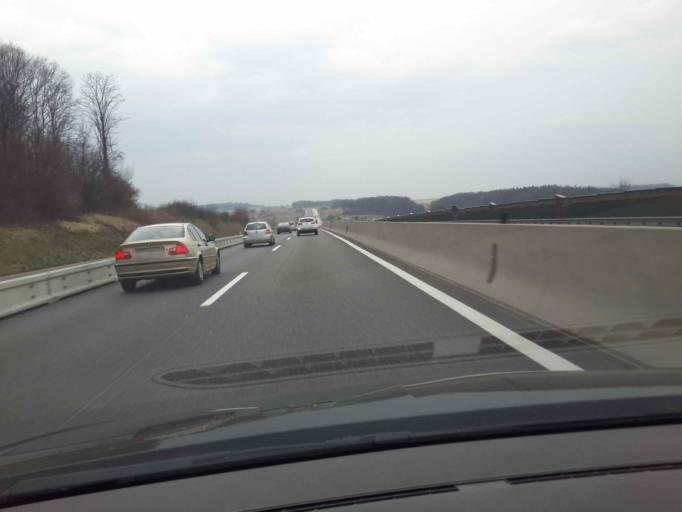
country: AT
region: Lower Austria
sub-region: Politischer Bezirk Sankt Polten
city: Boheimkirchen
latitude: 48.1864
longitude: 15.7400
